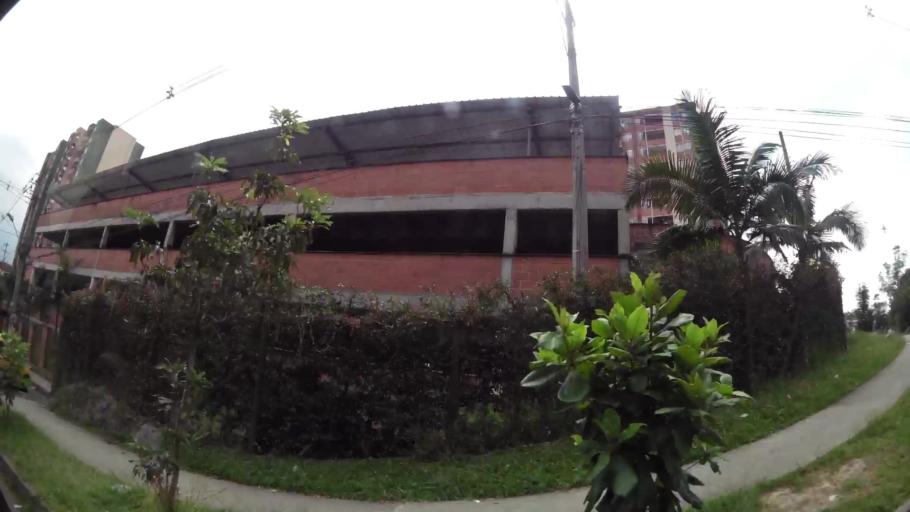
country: CO
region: Antioquia
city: Itagui
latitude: 6.1903
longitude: -75.6006
